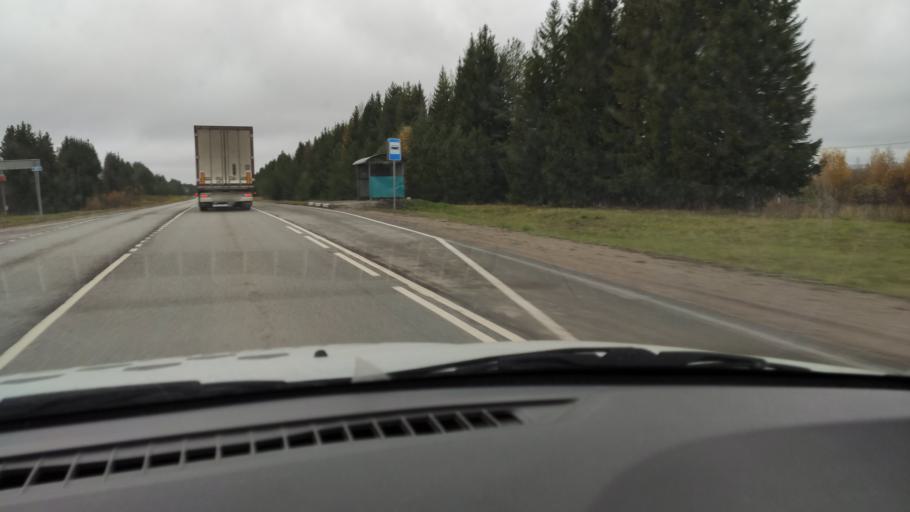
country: RU
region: Kirov
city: Slobodskoy
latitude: 58.7393
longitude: 50.2956
